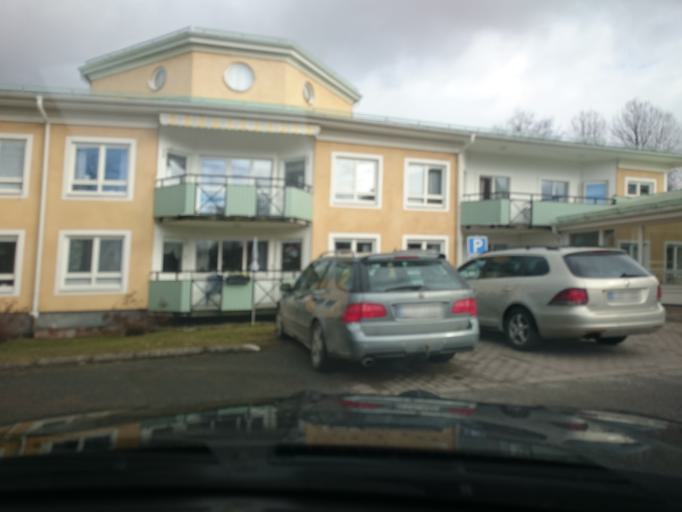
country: SE
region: Joenkoeping
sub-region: Vetlanda Kommun
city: Vetlanda
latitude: 57.3061
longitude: 15.1274
